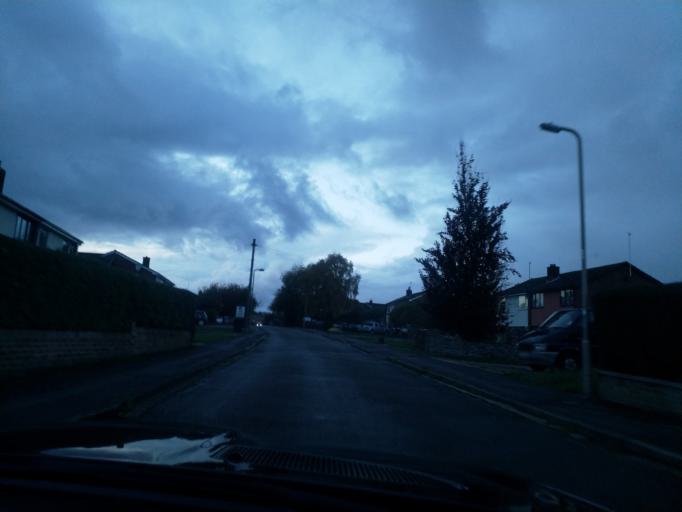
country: GB
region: England
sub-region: Oxfordshire
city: Wheatley
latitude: 51.7444
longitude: -1.1336
